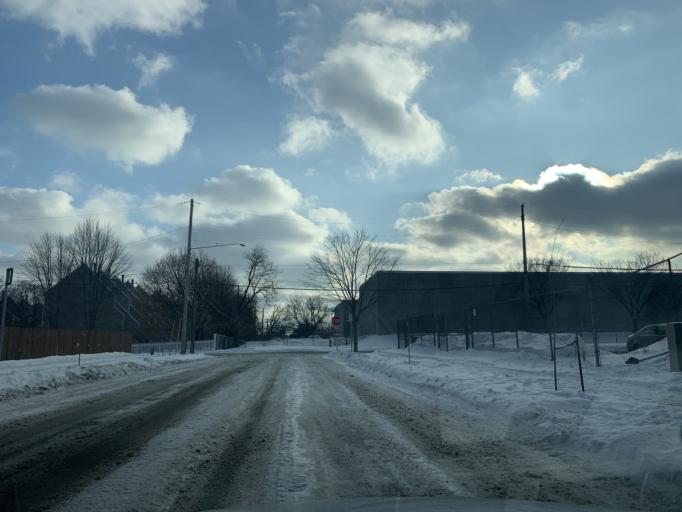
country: US
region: Minnesota
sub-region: Hennepin County
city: Minneapolis
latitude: 44.9936
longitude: -93.2896
